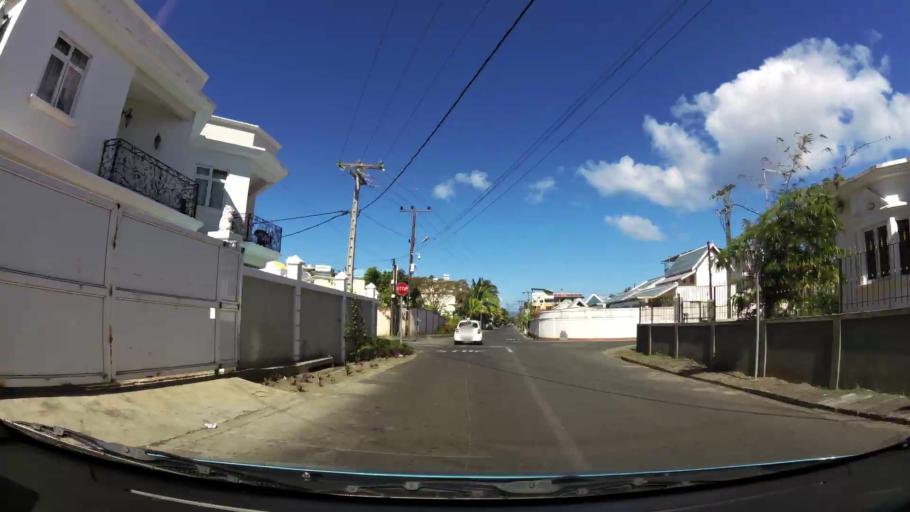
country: MU
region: Black River
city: Flic en Flac
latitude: -20.2851
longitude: 57.3676
